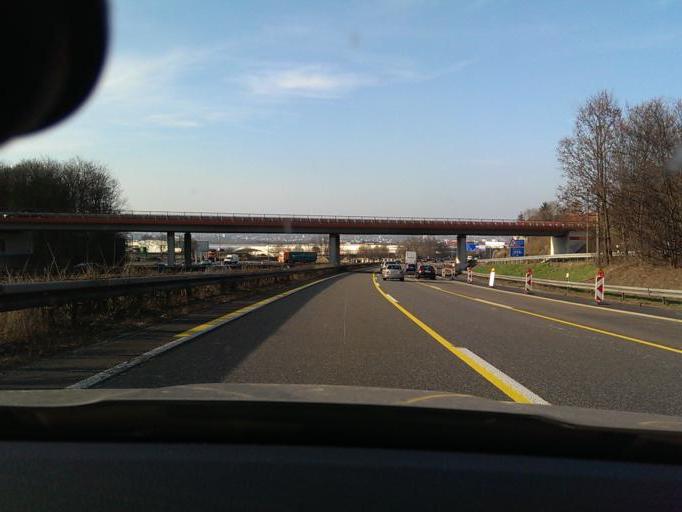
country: DE
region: Hesse
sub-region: Regierungsbezirk Kassel
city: Lohfelden
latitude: 51.2648
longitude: 9.5165
